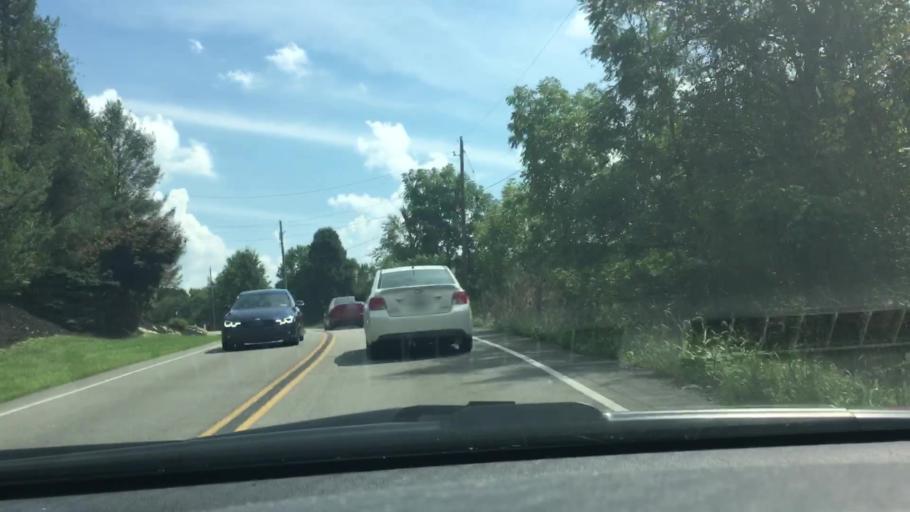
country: US
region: Pennsylvania
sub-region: Washington County
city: Thompsonville
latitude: 40.2501
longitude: -80.1176
